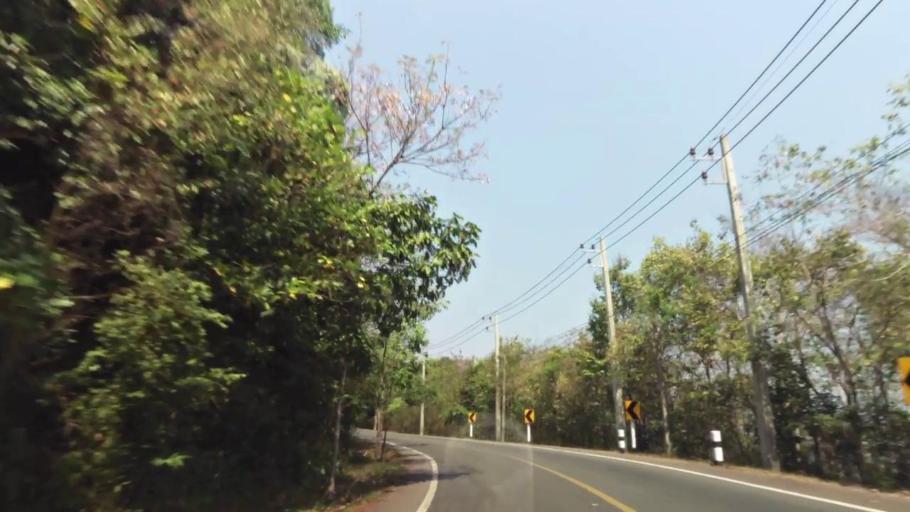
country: TH
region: Chanthaburi
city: Tha Mai
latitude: 12.5367
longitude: 101.9471
